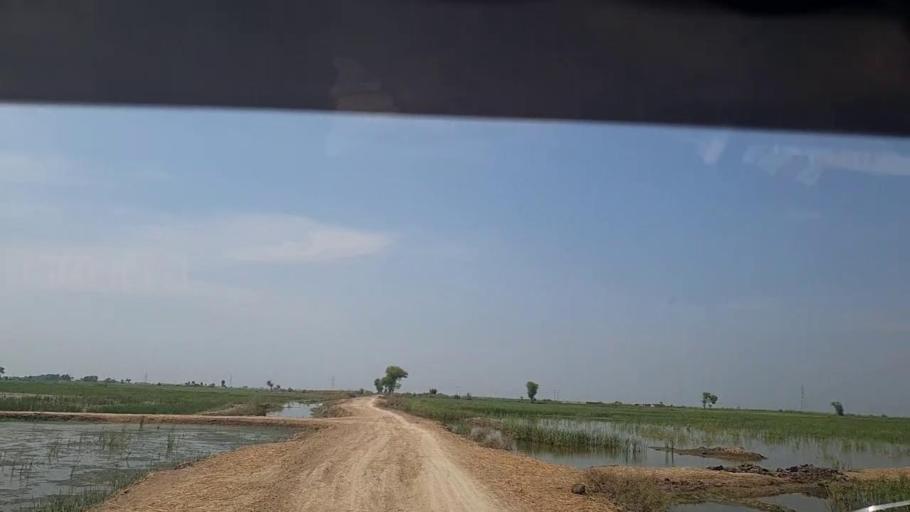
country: PK
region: Sindh
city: Thul
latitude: 28.2170
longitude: 68.6792
